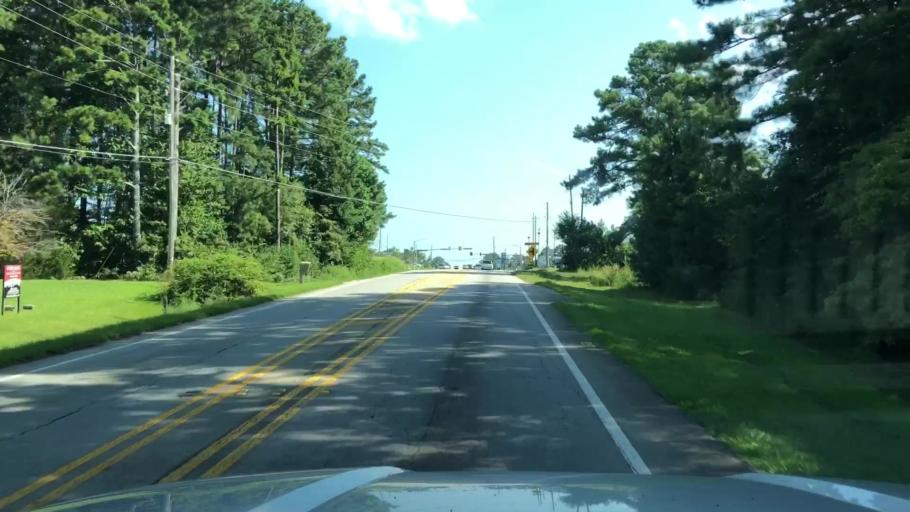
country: US
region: Georgia
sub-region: Cobb County
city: Acworth
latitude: 34.0079
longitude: -84.7567
